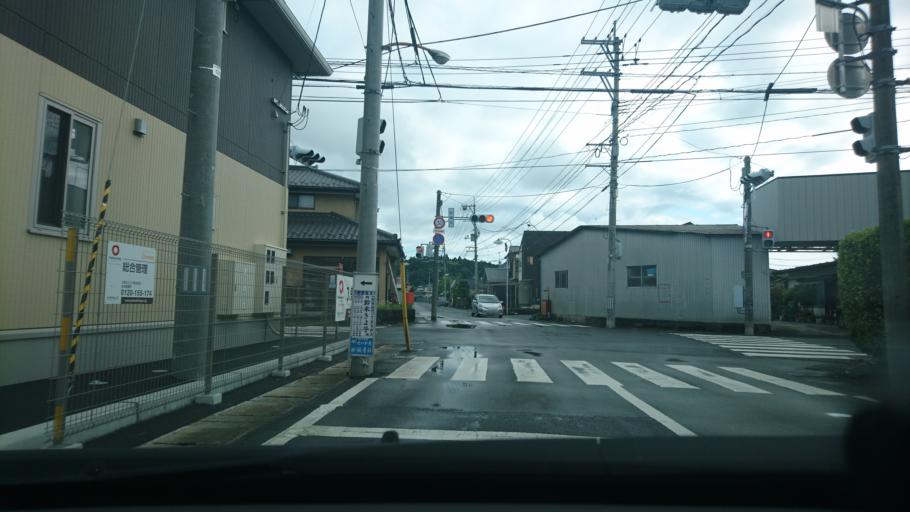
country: JP
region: Miyagi
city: Wakuya
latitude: 38.6544
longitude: 141.2768
